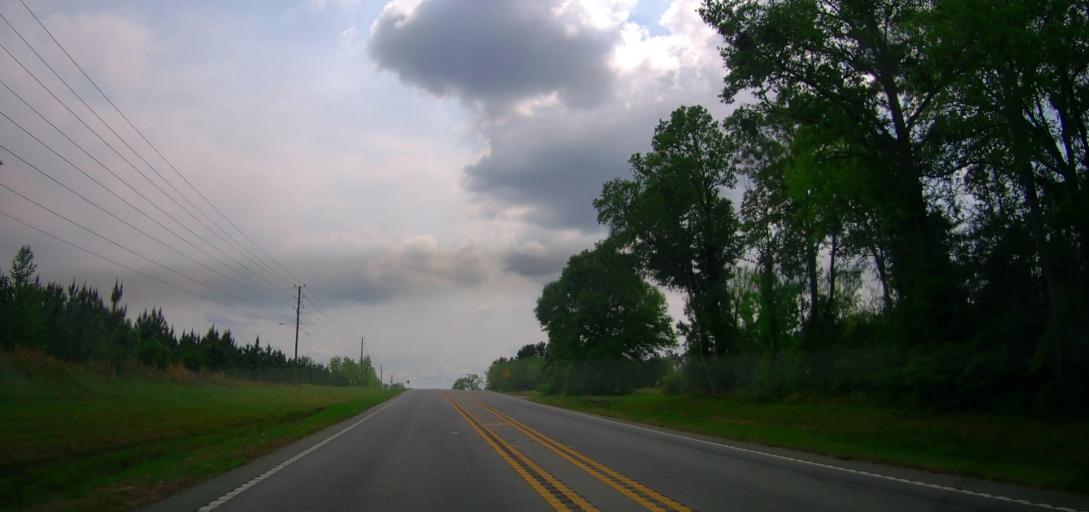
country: US
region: Georgia
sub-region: Treutlen County
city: Soperton
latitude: 32.3621
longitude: -82.5952
